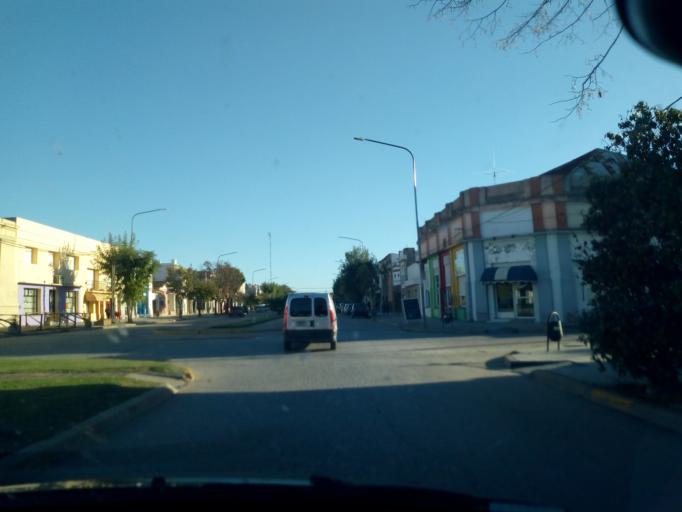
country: AR
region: Buenos Aires
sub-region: Partido de Loberia
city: Loberia
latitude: -38.1607
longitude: -58.7797
